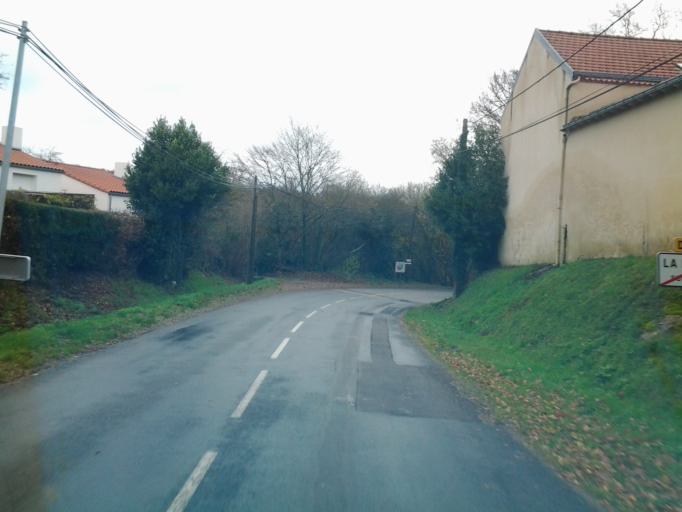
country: FR
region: Pays de la Loire
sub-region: Departement de la Vendee
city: La Roche-sur-Yon
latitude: 46.6594
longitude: -1.3994
